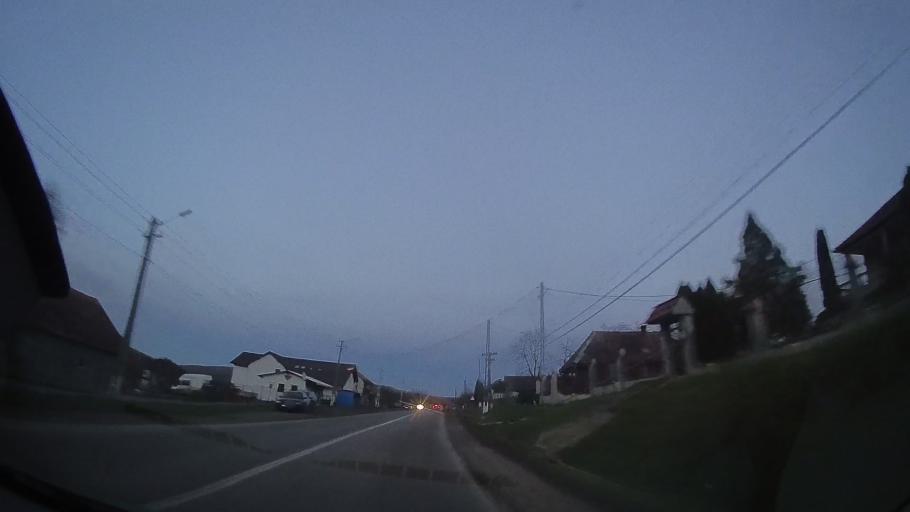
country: RO
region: Cluj
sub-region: Comuna Camarasu
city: Camarasu
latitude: 46.7937
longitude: 24.1307
